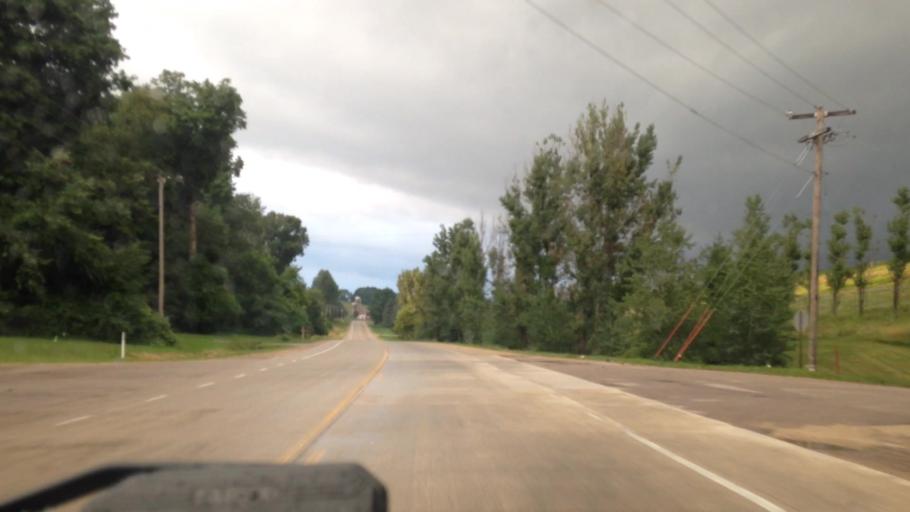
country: US
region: Wisconsin
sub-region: Dodge County
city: Mayville
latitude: 43.4576
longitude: -88.5614
